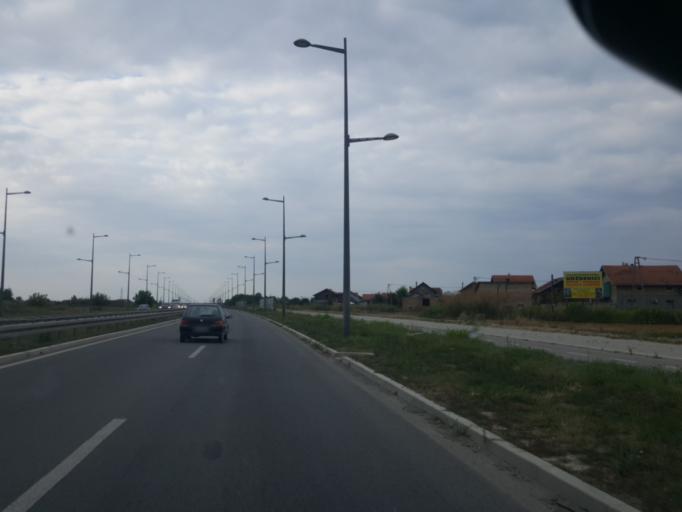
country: RS
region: Autonomna Pokrajina Vojvodina
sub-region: Juznobacki Okrug
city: Novi Sad
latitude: 45.2932
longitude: 19.8077
